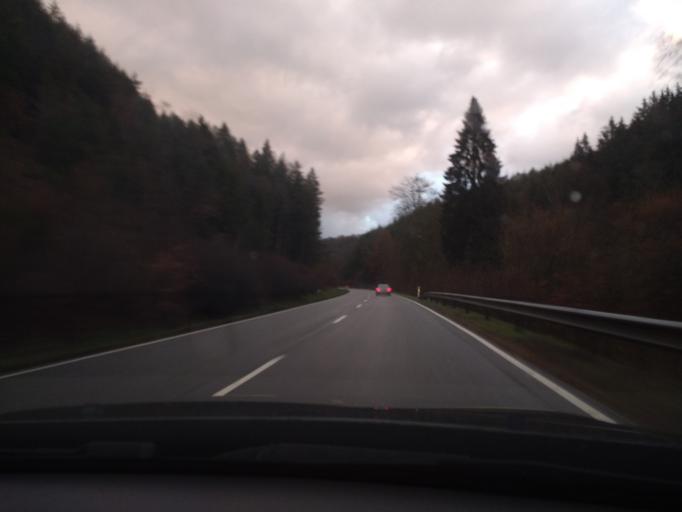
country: DE
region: Rheinland-Pfalz
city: Breit
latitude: 49.7636
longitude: 6.9039
